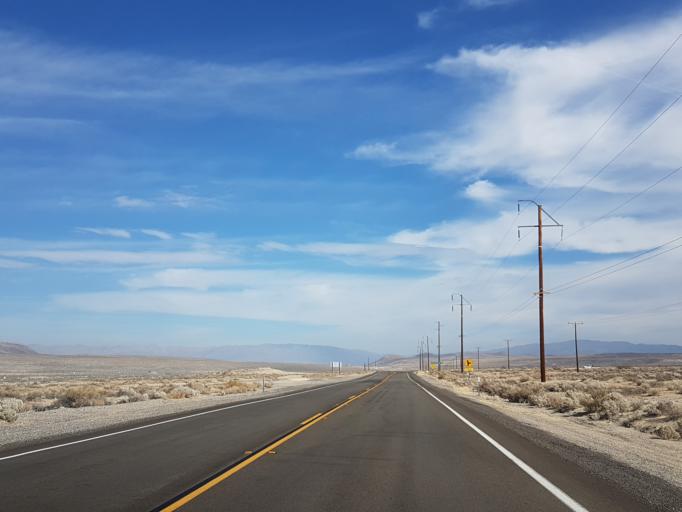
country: US
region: California
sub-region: Kern County
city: Ridgecrest
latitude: 35.6467
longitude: -117.5138
